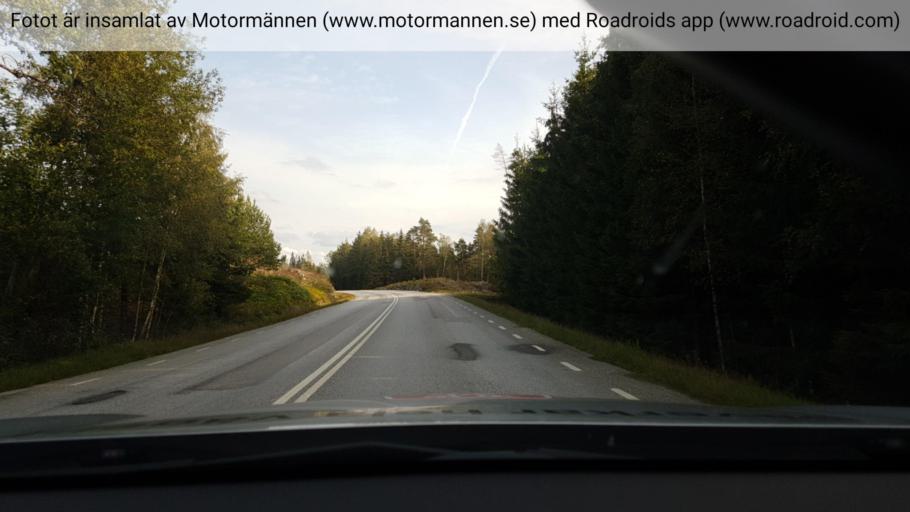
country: SE
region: Vaestra Goetaland
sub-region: Uddevalla Kommun
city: Ljungskile
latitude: 58.1547
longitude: 11.9724
